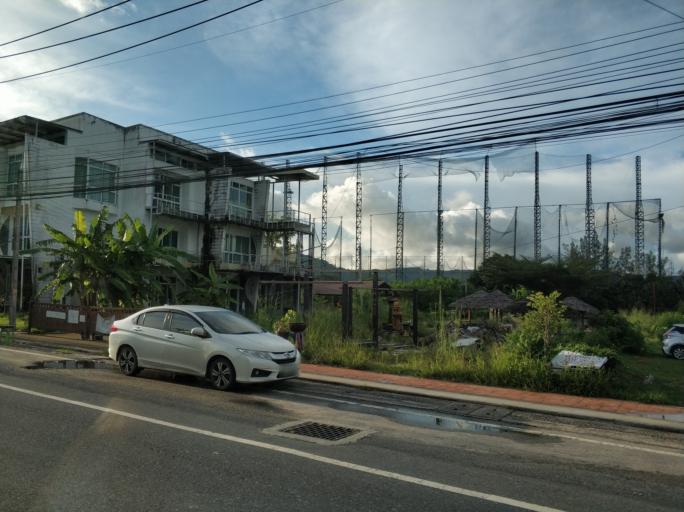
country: TH
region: Phuket
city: Kathu
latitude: 7.8996
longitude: 98.3472
